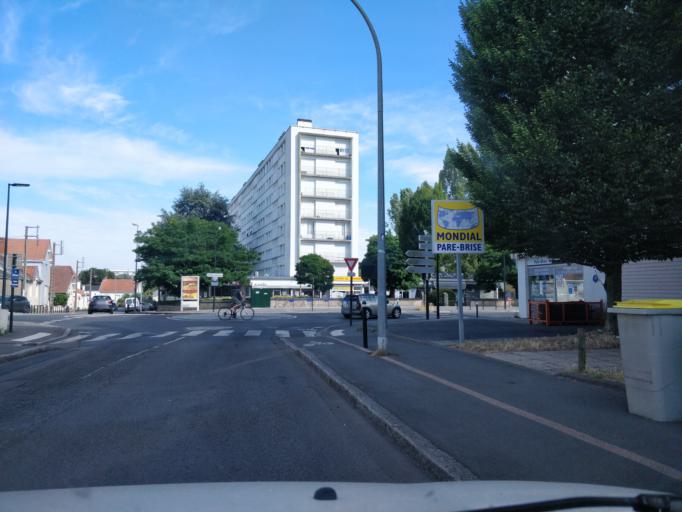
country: FR
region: Pays de la Loire
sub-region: Departement de la Loire-Atlantique
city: Nantes
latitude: 47.2409
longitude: -1.5307
